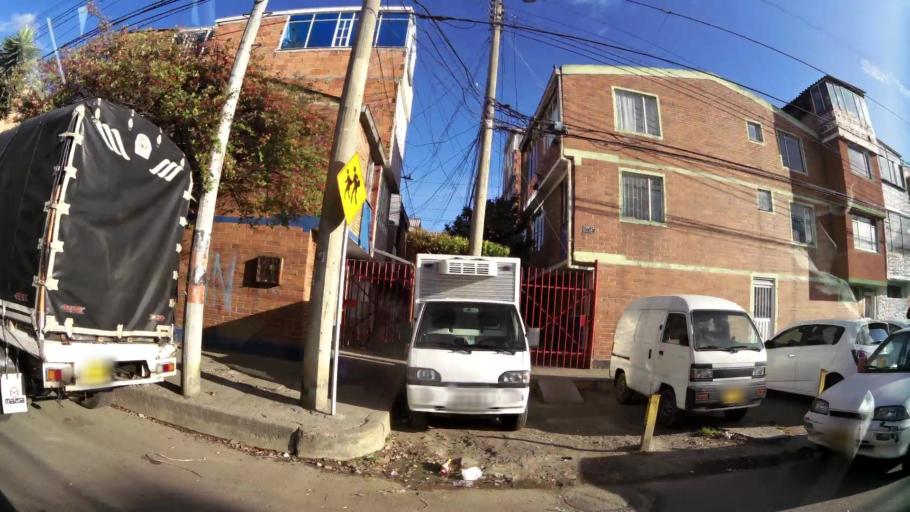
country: CO
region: Cundinamarca
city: Soacha
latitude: 4.5770
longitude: -74.1523
